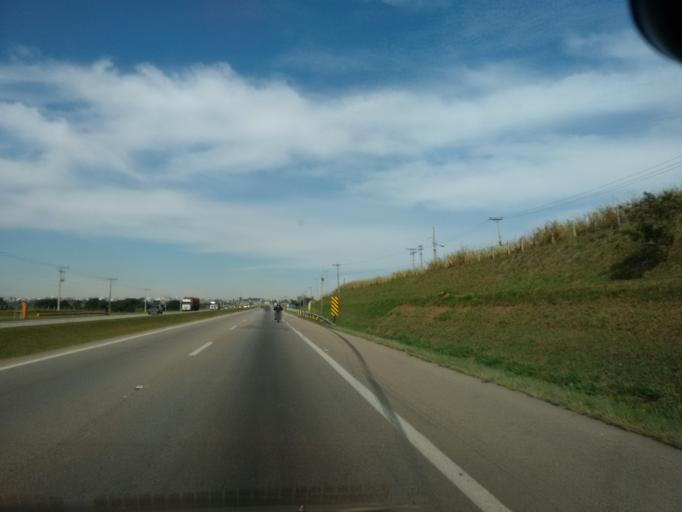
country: BR
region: Sao Paulo
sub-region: Itu
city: Itu
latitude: -23.2873
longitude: -47.3295
